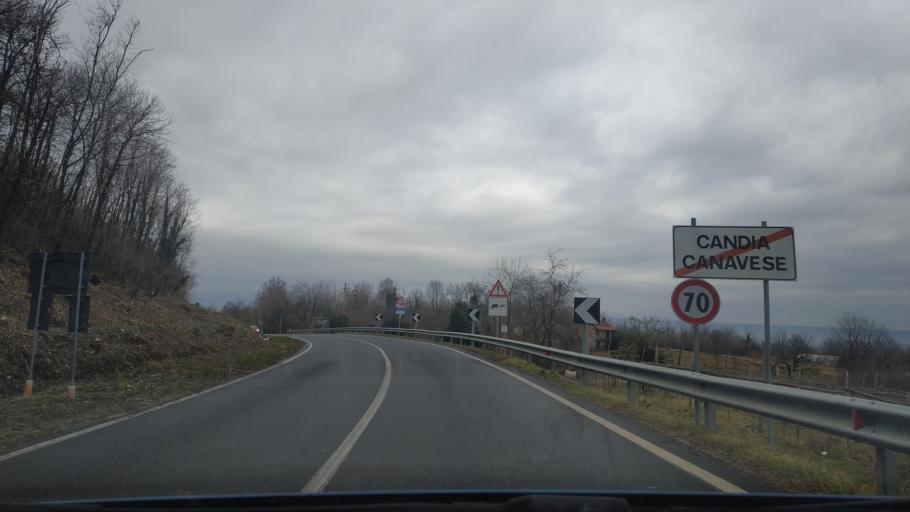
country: IT
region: Piedmont
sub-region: Provincia di Torino
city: Candia Canavese
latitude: 45.3359
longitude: 7.8903
